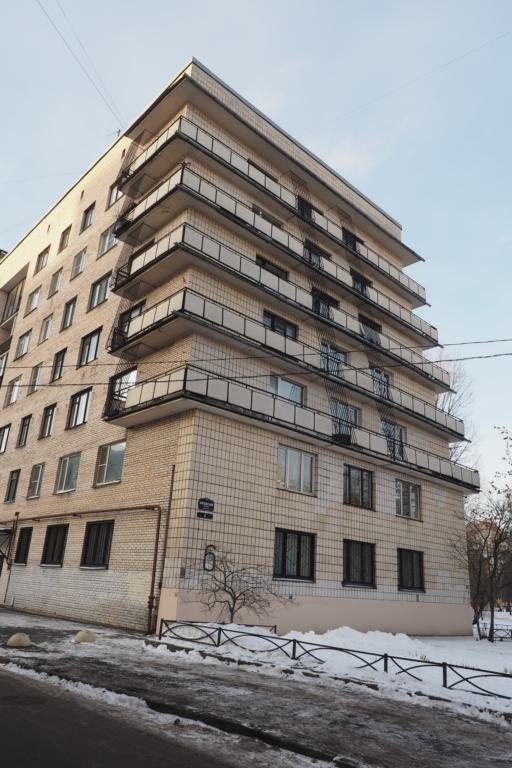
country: RU
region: St.-Petersburg
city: Petrogradka
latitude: 59.9730
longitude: 30.3006
